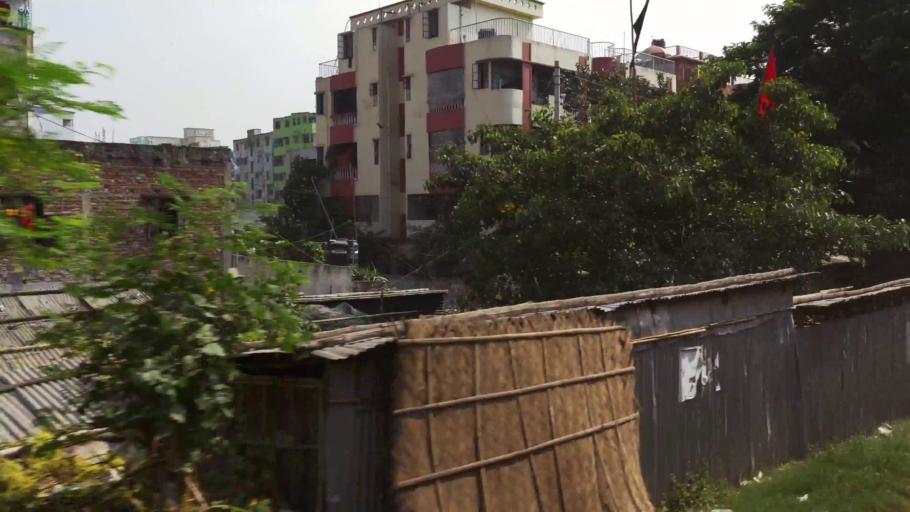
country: BD
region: Dhaka
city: Paltan
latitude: 23.8098
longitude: 90.4032
